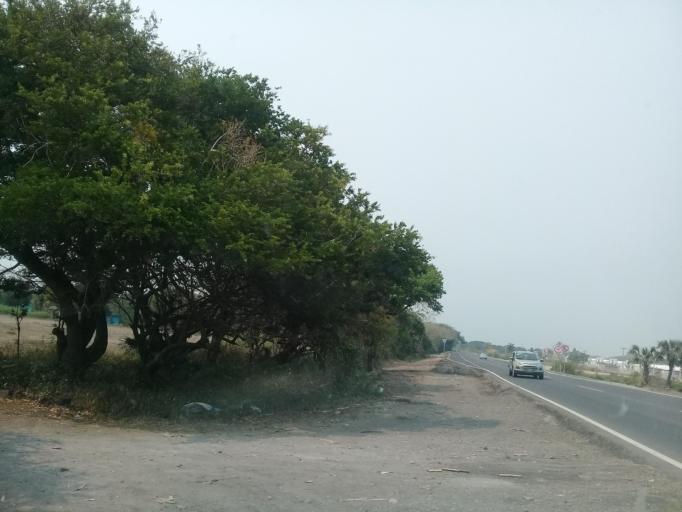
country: MX
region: Veracruz
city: Paso del Toro
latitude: 18.9825
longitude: -96.1738
